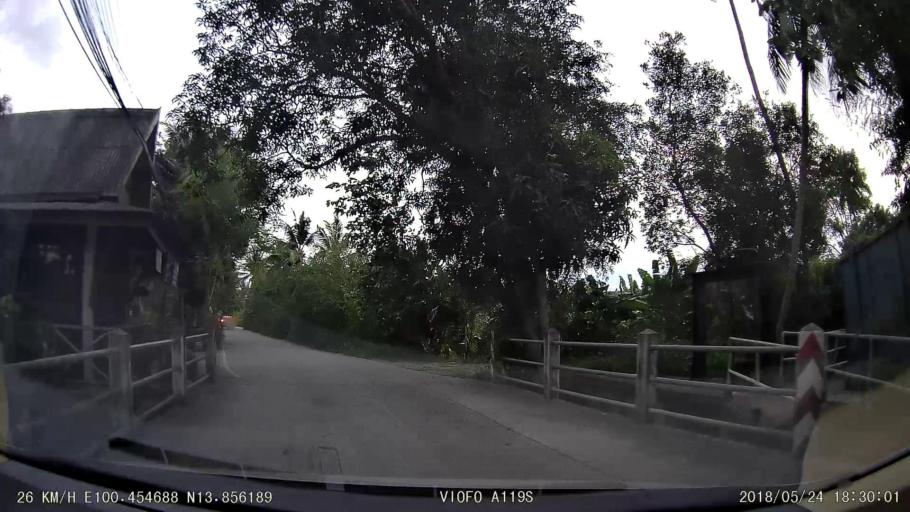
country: TH
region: Nonthaburi
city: Bang Kruai
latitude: 13.8563
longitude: 100.4545
